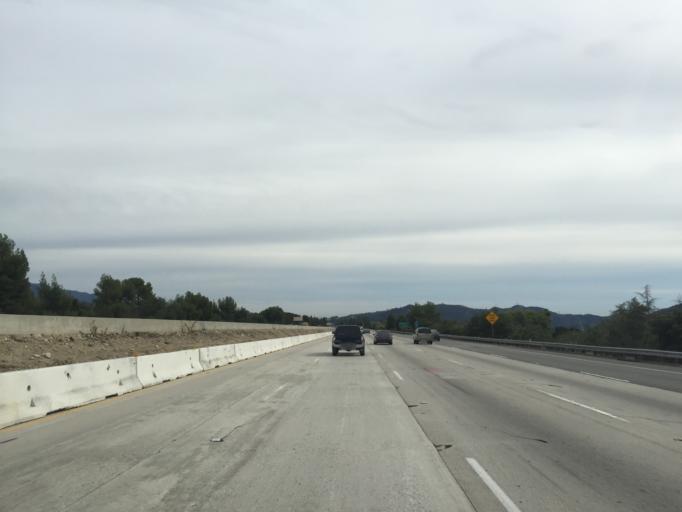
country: US
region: California
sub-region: Los Angeles County
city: La Crescenta-Montrose
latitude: 34.2282
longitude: -118.2573
